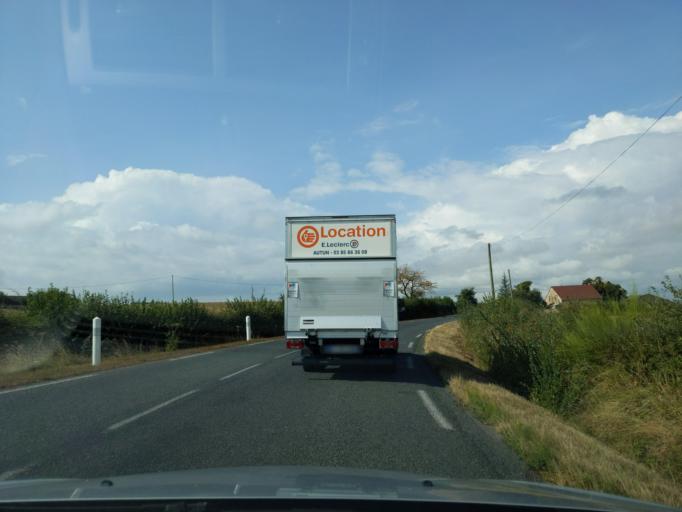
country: FR
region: Bourgogne
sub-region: Departement de Saone-et-Loire
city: Bourbon-Lancy
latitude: 46.6465
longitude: 3.7813
